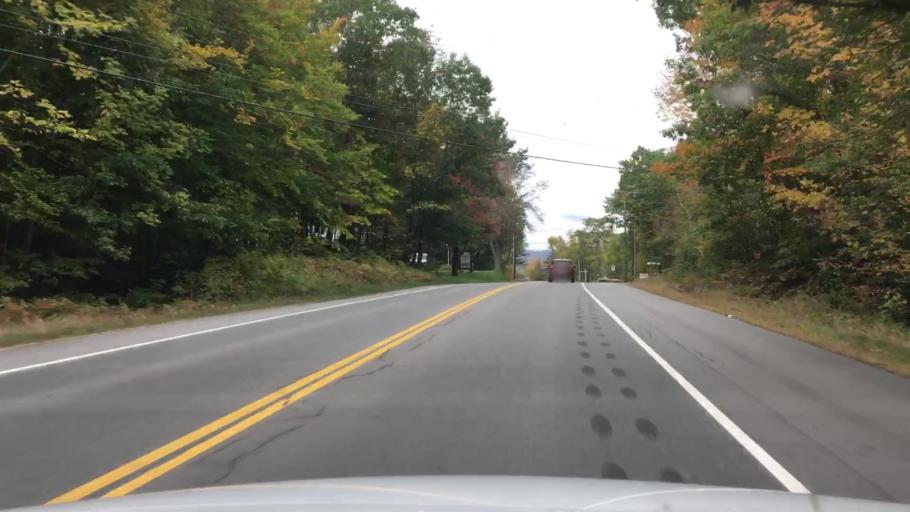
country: US
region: New Hampshire
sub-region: Coos County
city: Gorham
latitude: 44.4005
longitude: -71.1110
